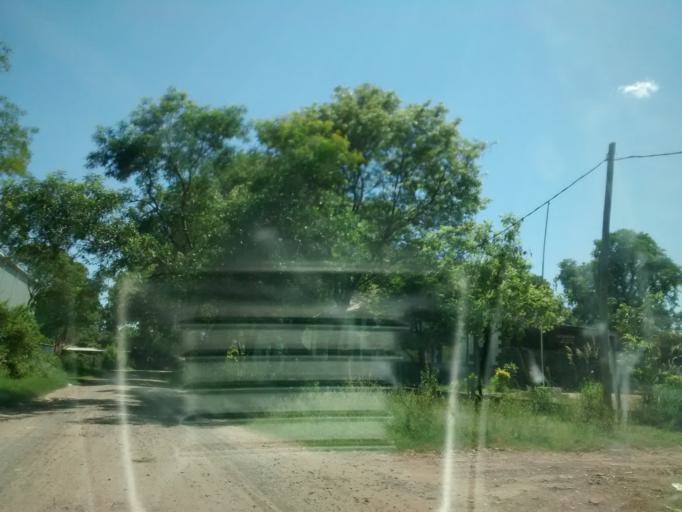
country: AR
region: Chaco
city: Fontana
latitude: -27.4104
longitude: -59.0007
